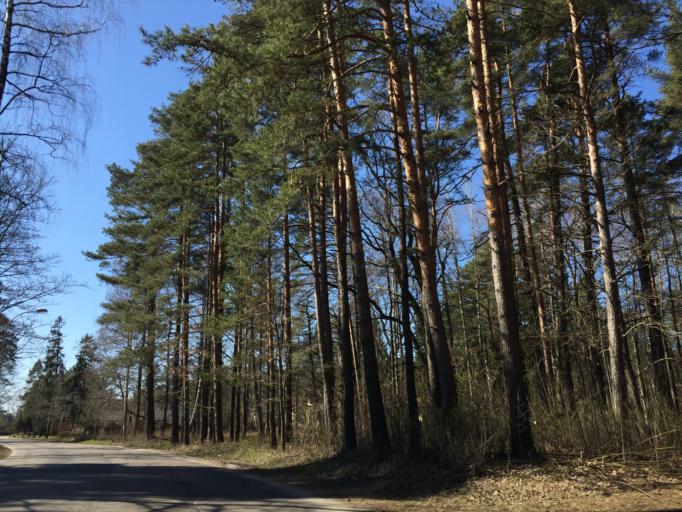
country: LV
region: Jurmala
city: Jurmala
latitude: 56.9483
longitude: 23.7442
